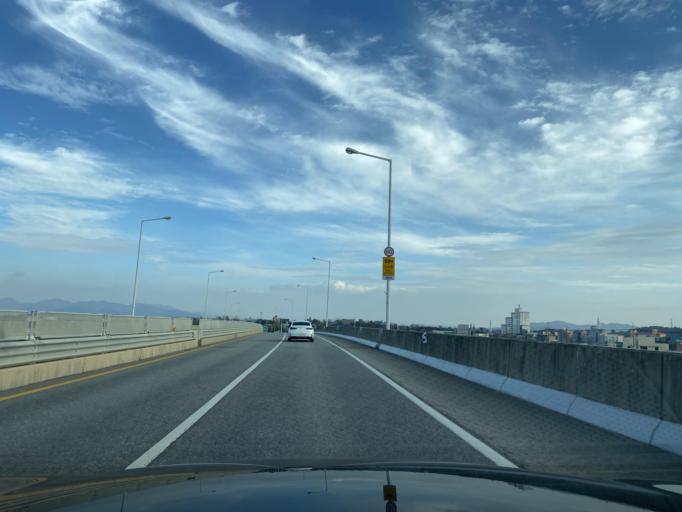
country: KR
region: Chungcheongnam-do
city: Yesan
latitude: 36.6913
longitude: 126.7375
